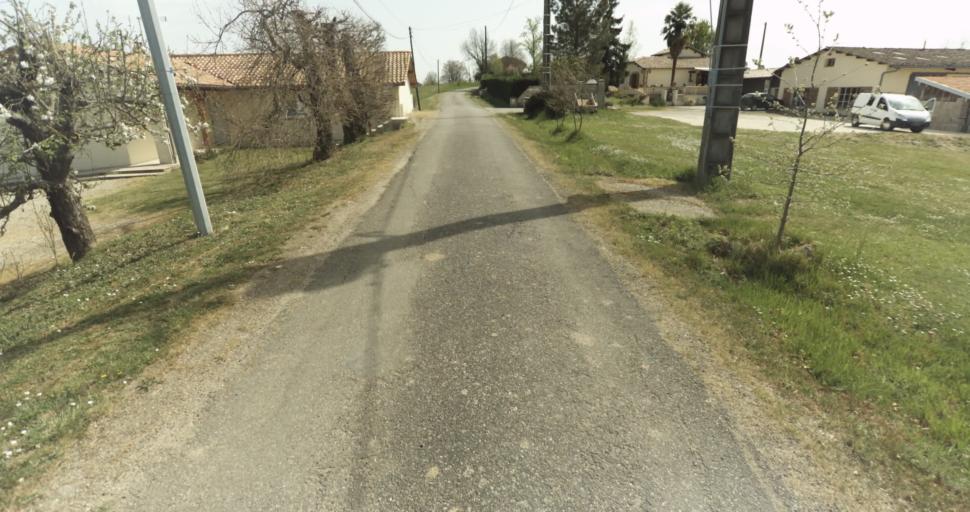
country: FR
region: Midi-Pyrenees
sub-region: Departement du Tarn-et-Garonne
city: Moissac
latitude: 44.1596
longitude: 1.0782
